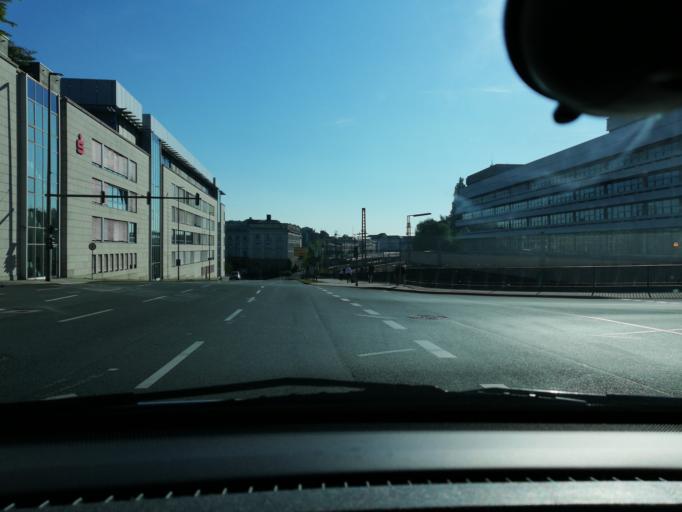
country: DE
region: North Rhine-Westphalia
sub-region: Regierungsbezirk Dusseldorf
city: Wuppertal
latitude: 51.2532
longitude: 7.1449
